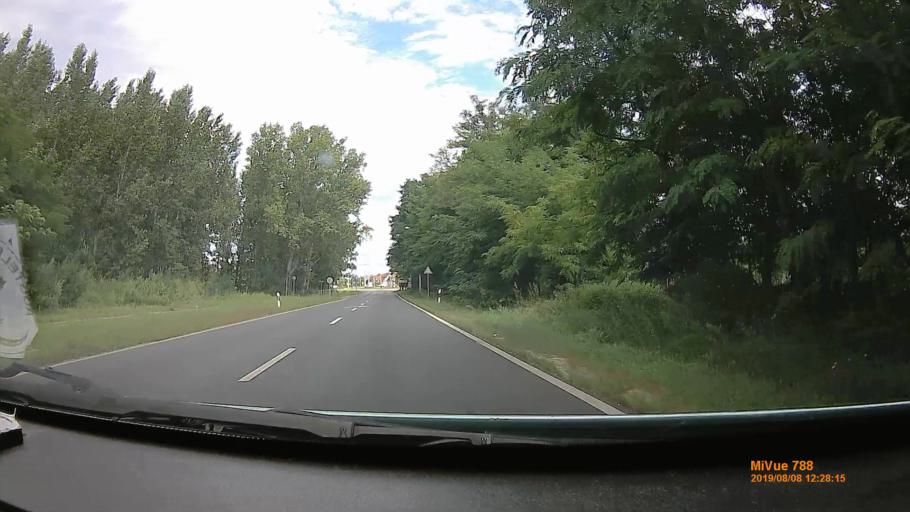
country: HU
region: Szabolcs-Szatmar-Bereg
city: Nyirbator
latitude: 47.8284
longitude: 22.1111
